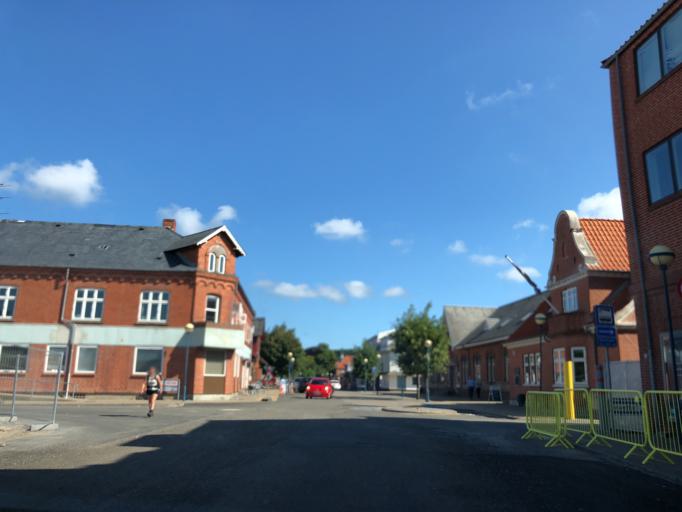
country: DK
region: North Denmark
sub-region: Jammerbugt Kommune
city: Fjerritslev
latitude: 57.0863
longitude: 9.2660
